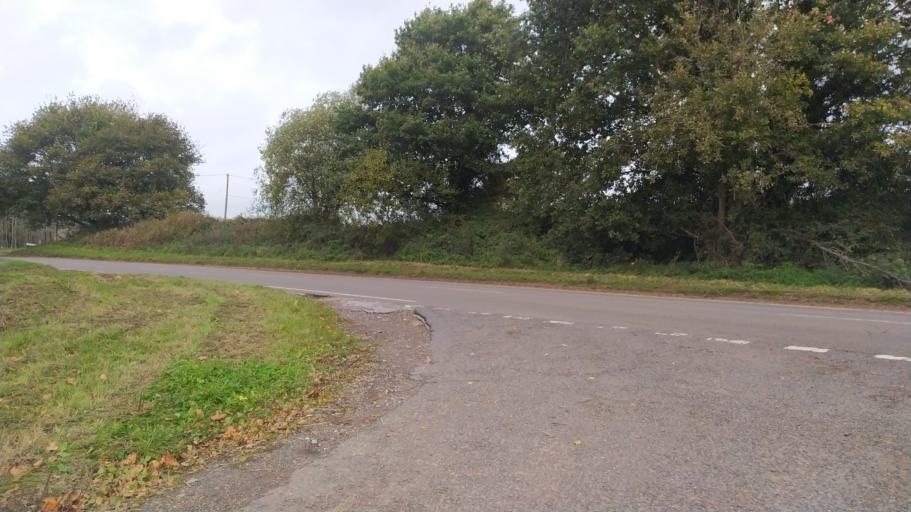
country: GB
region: England
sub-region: Hampshire
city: Liss
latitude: 51.0065
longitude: -0.8689
